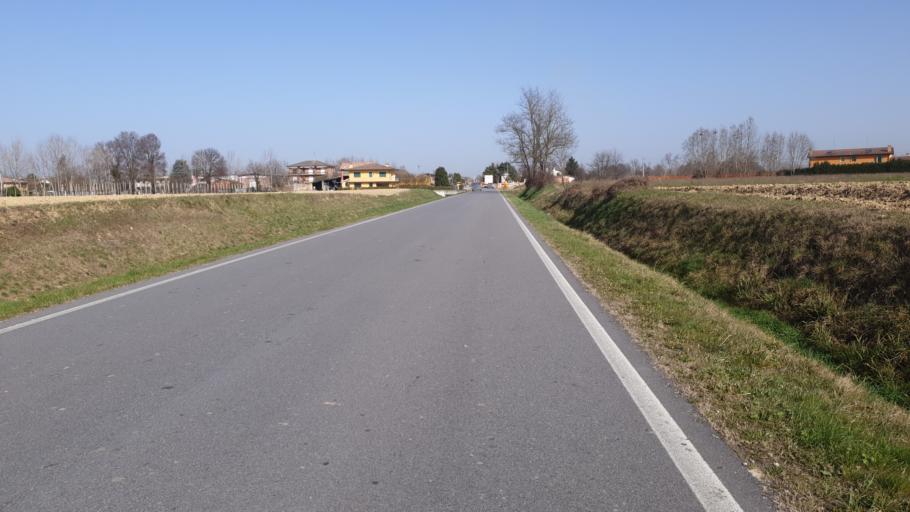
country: IT
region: Veneto
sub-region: Provincia di Padova
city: Cavino
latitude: 45.5106
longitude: 11.8911
